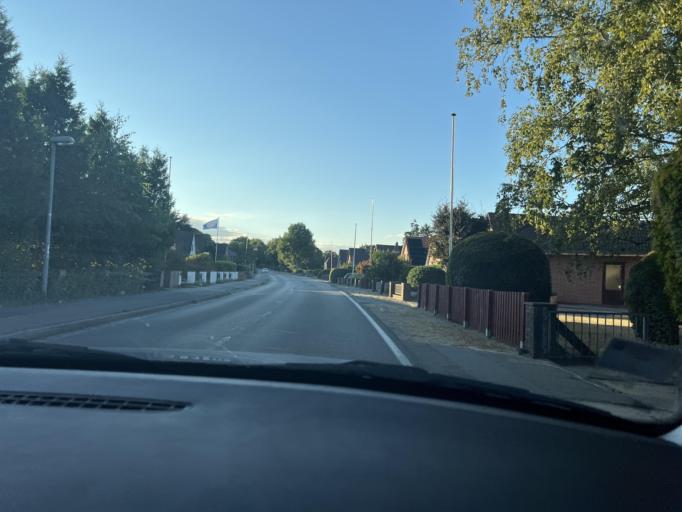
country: DE
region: Schleswig-Holstein
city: Suderheistedt
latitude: 54.2218
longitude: 9.1215
